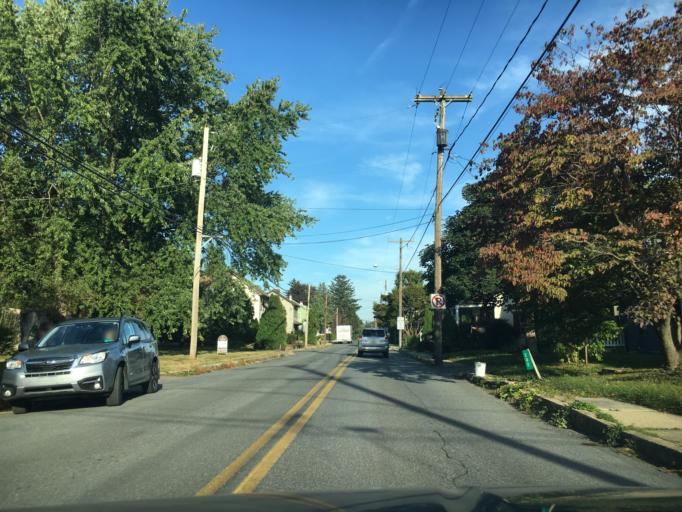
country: US
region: Pennsylvania
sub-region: Lancaster County
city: Brownstown
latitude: 40.1258
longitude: -76.2064
